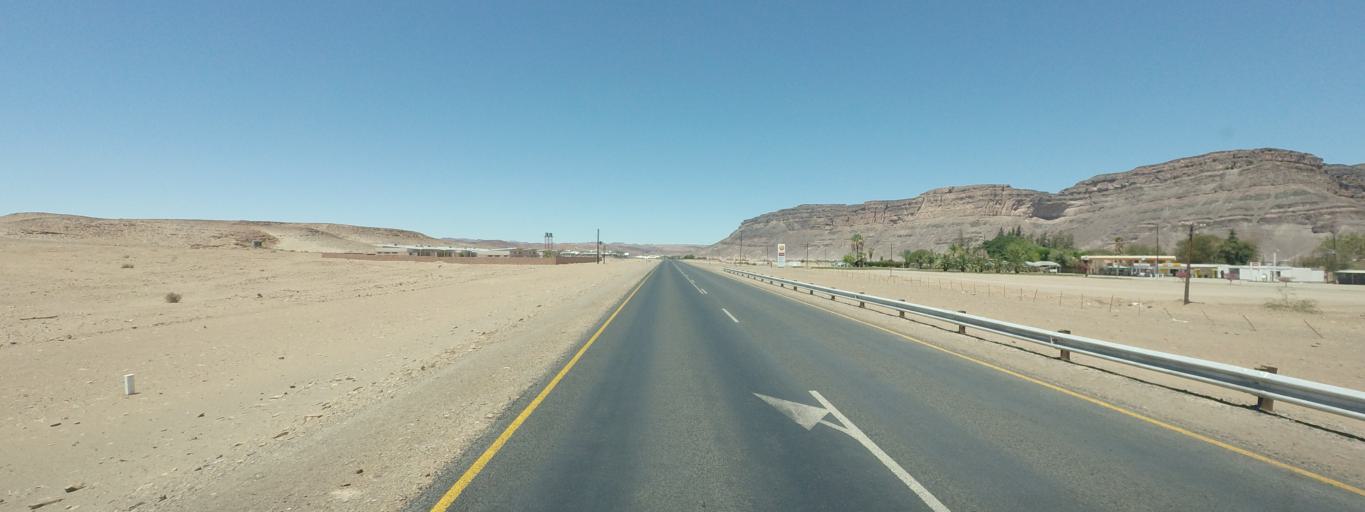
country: ZA
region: Northern Cape
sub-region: Namakwa District Municipality
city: Port Nolloth
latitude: -28.7420
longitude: 17.6175
